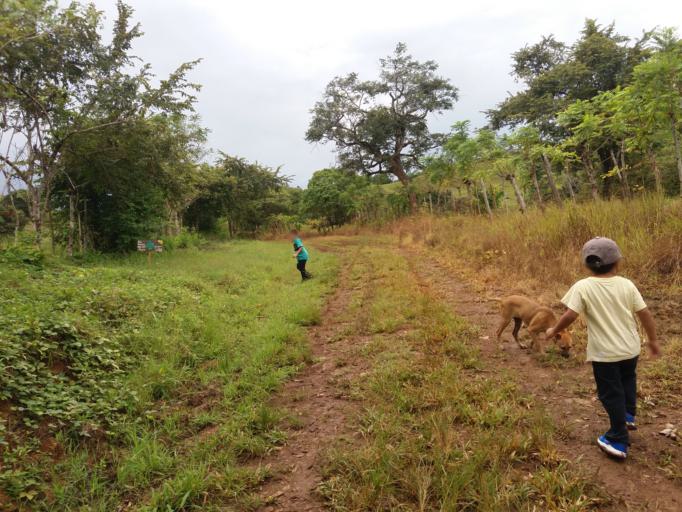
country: PA
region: Los Santos
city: Bella Vista
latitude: 7.6254
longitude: -80.1668
